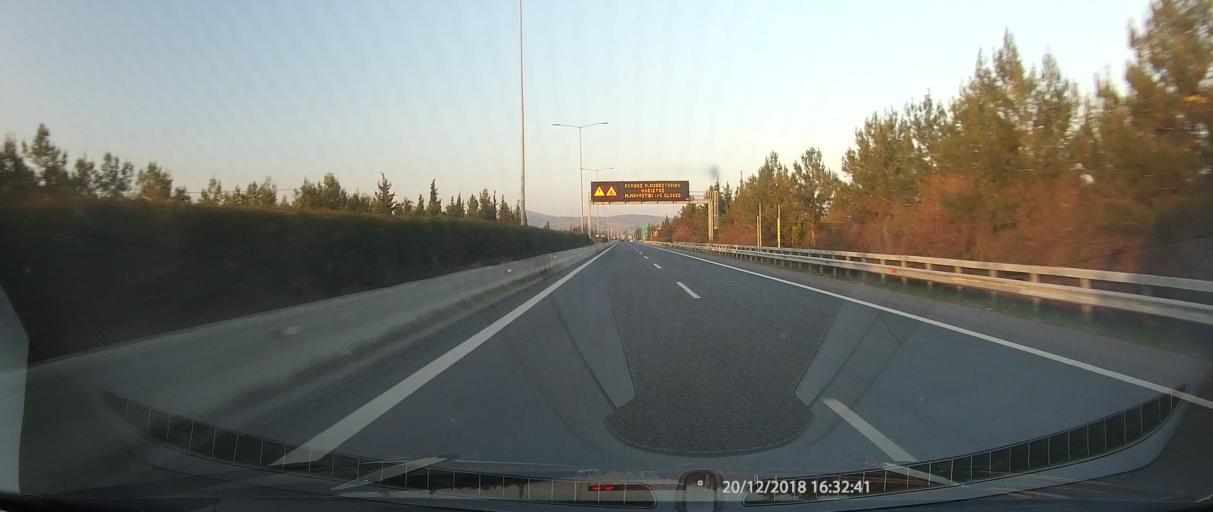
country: GR
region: Thessaly
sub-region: Nomos Magnisias
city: Evxinoupolis
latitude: 39.2494
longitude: 22.7349
